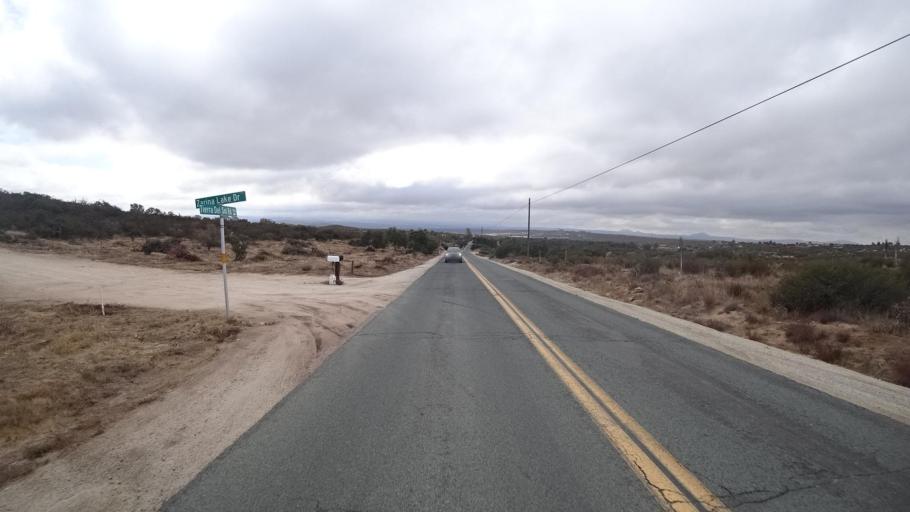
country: US
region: California
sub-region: San Diego County
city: Campo
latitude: 32.6349
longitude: -116.3202
